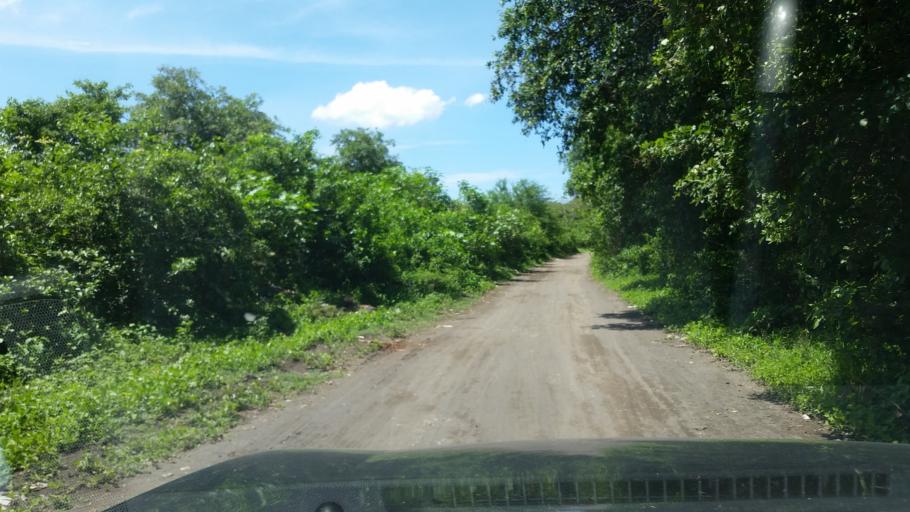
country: NI
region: Chinandega
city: Puerto Morazan
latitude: 12.7640
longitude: -87.1337
